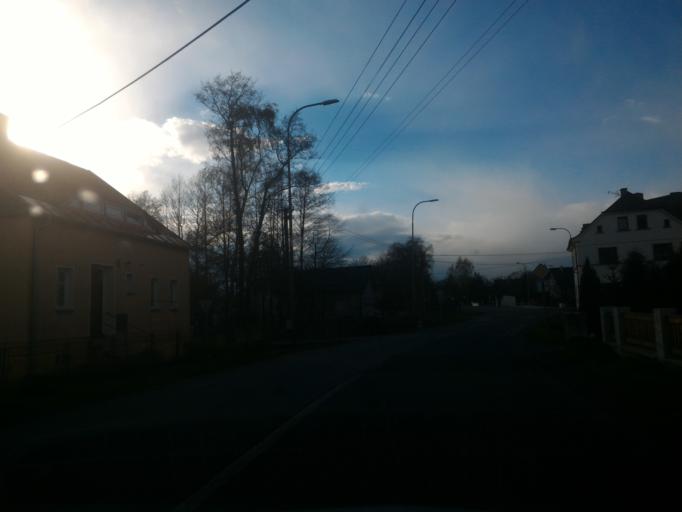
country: CZ
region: Ustecky
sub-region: Okres Decin
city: Krasna Lipa
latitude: 50.8809
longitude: 14.5464
